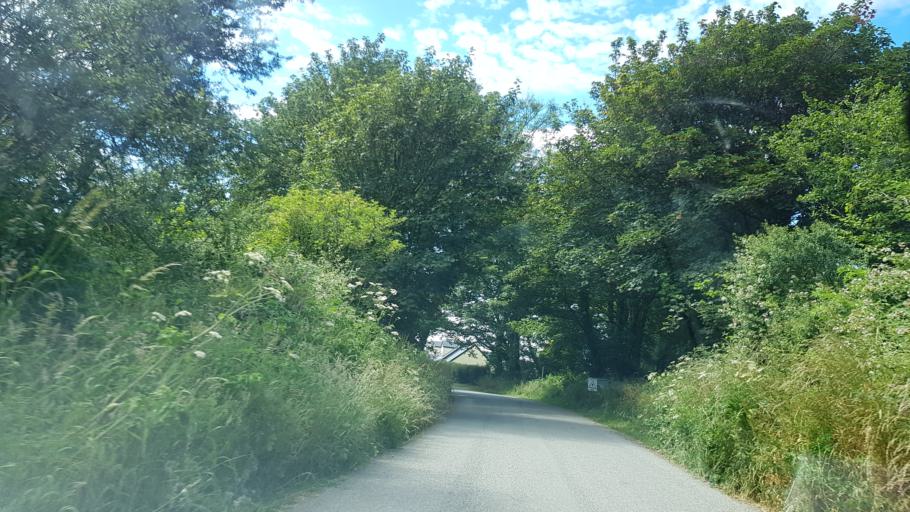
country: GB
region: Wales
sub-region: Pembrokeshire
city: Wiston
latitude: 51.8277
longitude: -4.8803
